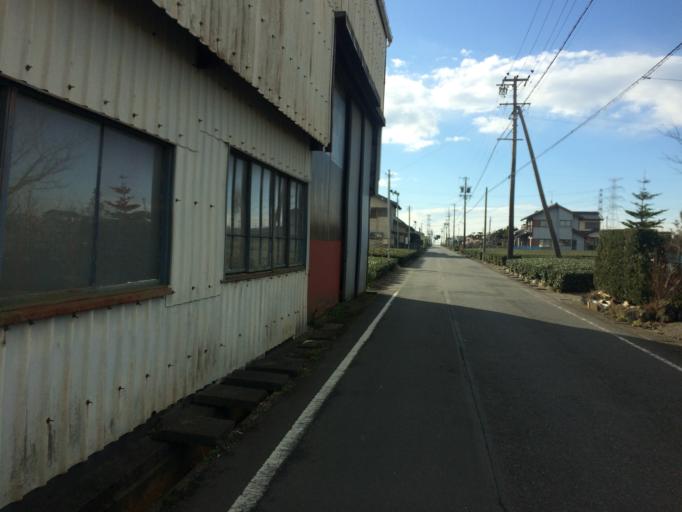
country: JP
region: Shizuoka
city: Kanaya
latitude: 34.7645
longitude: 138.1447
